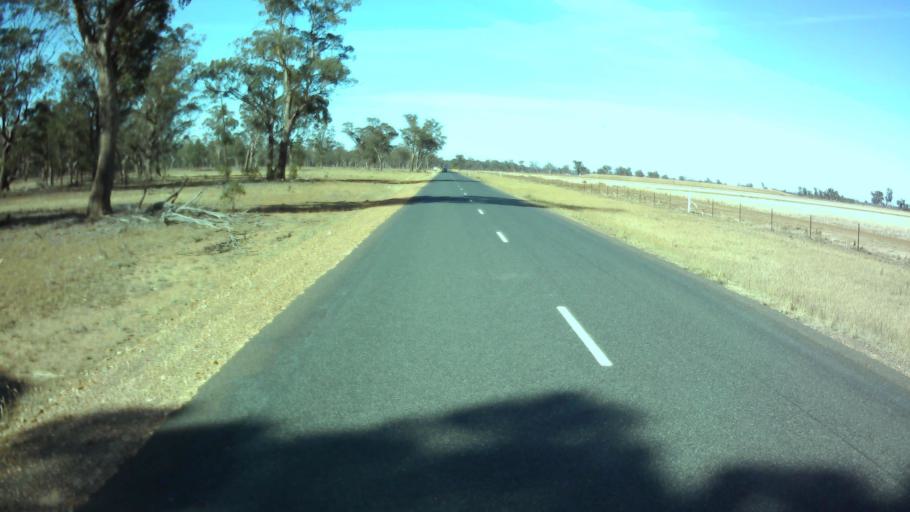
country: AU
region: New South Wales
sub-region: Weddin
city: Grenfell
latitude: -34.1249
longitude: 147.8049
